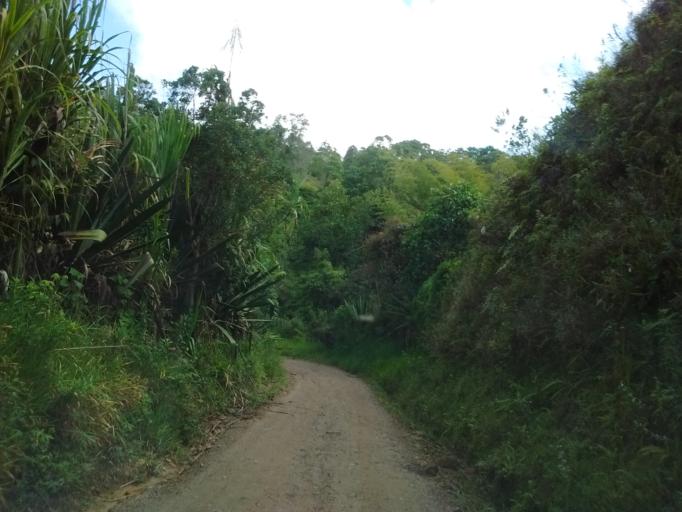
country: CO
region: Cauca
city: Morales
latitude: 2.6870
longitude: -76.7328
